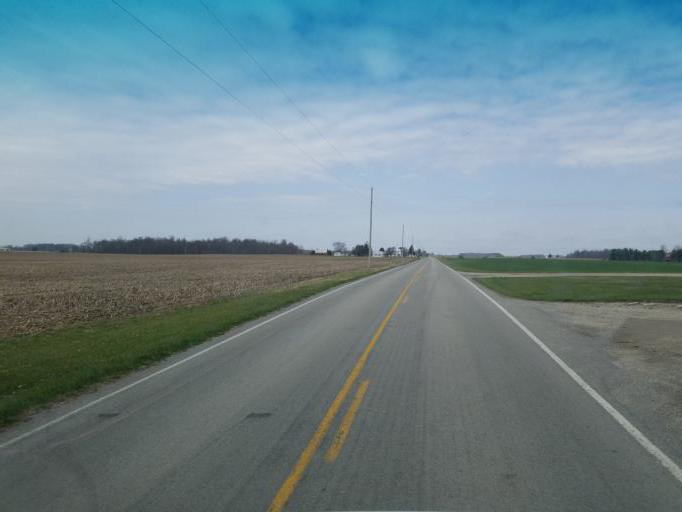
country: US
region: Ohio
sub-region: Wyandot County
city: Upper Sandusky
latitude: 40.8856
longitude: -83.1701
